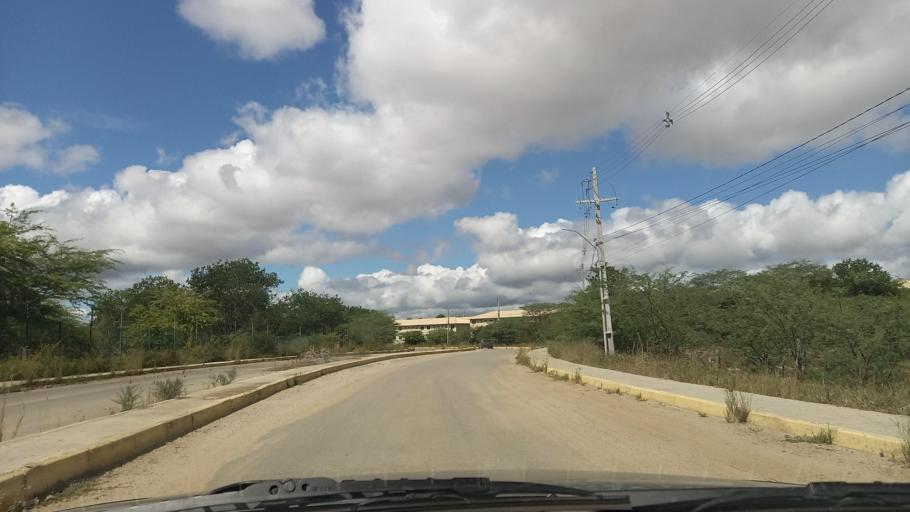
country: BR
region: Pernambuco
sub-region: Caruaru
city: Caruaru
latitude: -8.2428
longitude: -35.9845
